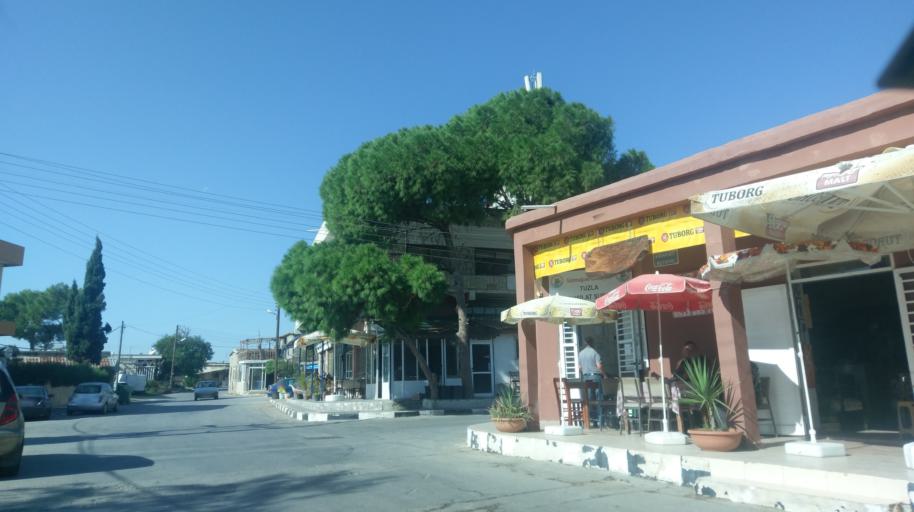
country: CY
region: Ammochostos
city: Acheritou
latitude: 35.1620
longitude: 33.8834
